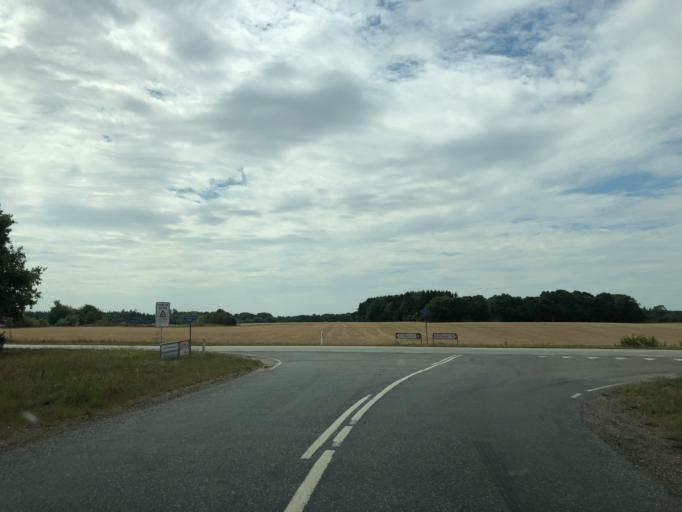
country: DK
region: South Denmark
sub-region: Vejle Kommune
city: Egtved
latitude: 55.6358
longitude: 9.2521
